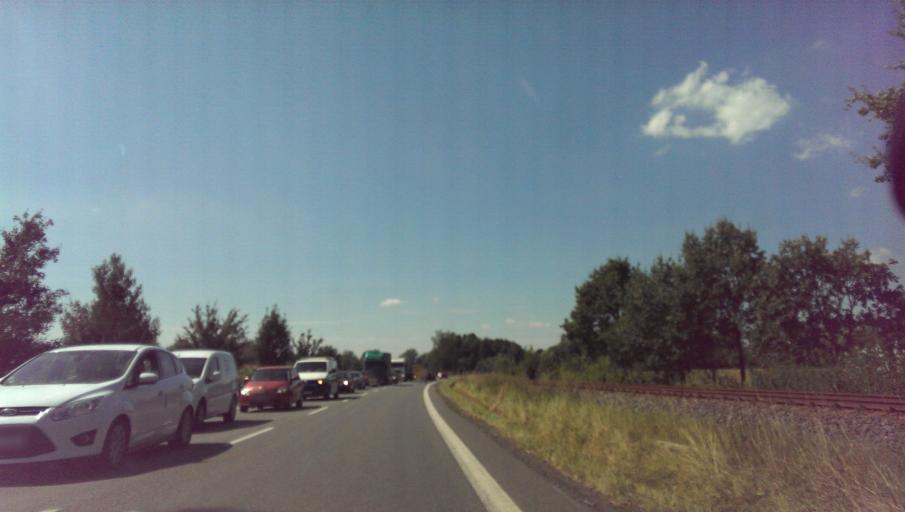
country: CZ
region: Zlin
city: Zubri
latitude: 49.4622
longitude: 18.0751
